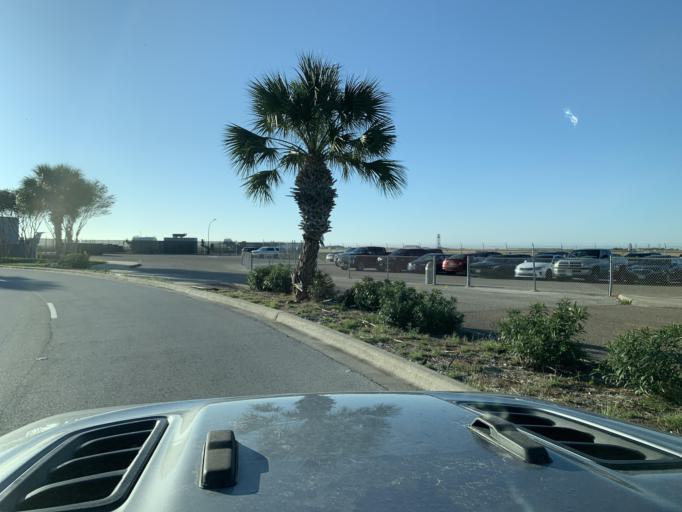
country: US
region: Texas
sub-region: Nueces County
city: Corpus Christi
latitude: 27.7751
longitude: -97.5041
